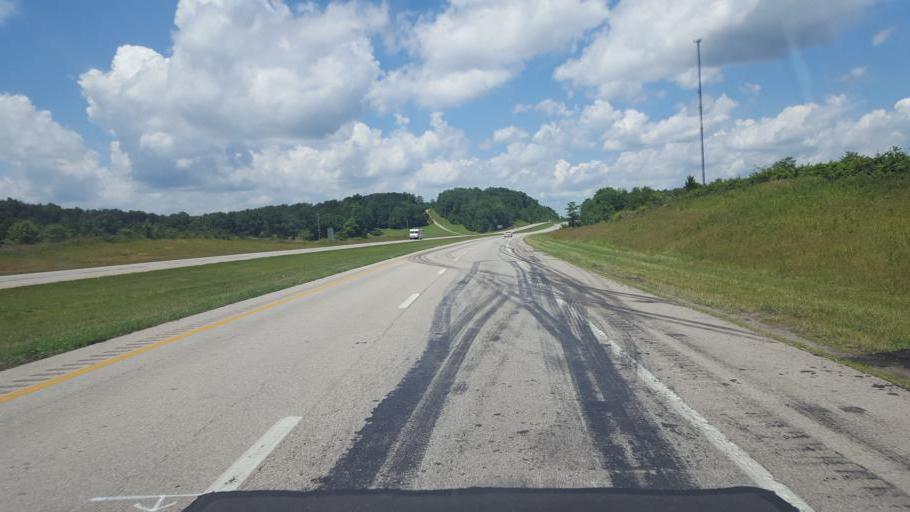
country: US
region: Ohio
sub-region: Gallia County
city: Gallipolis
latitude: 38.8842
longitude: -82.3398
